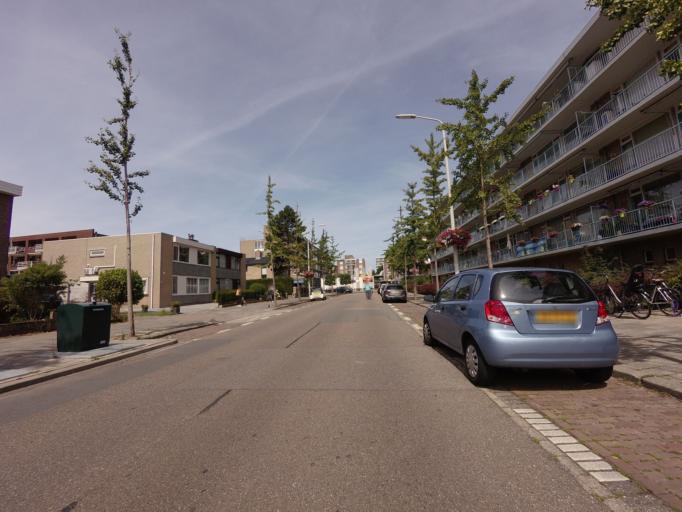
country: NL
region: South Holland
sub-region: Gemeente Westland
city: Poeldijk
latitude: 52.0521
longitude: 4.2354
